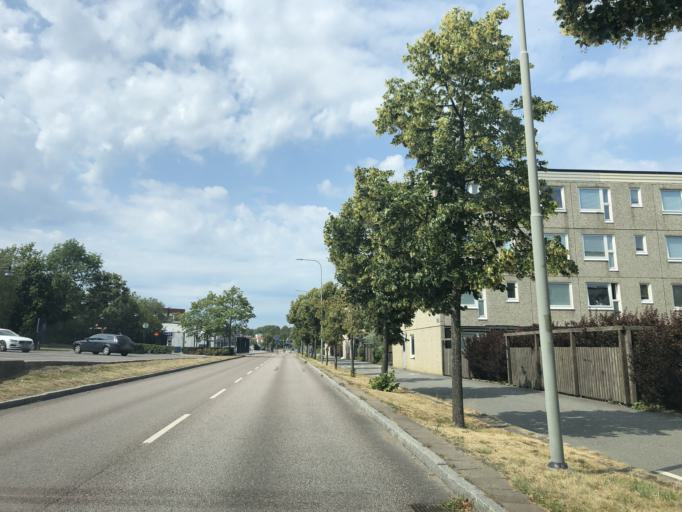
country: SE
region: Vaestra Goetaland
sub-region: Goteborg
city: Majorna
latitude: 57.7151
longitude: 11.9251
